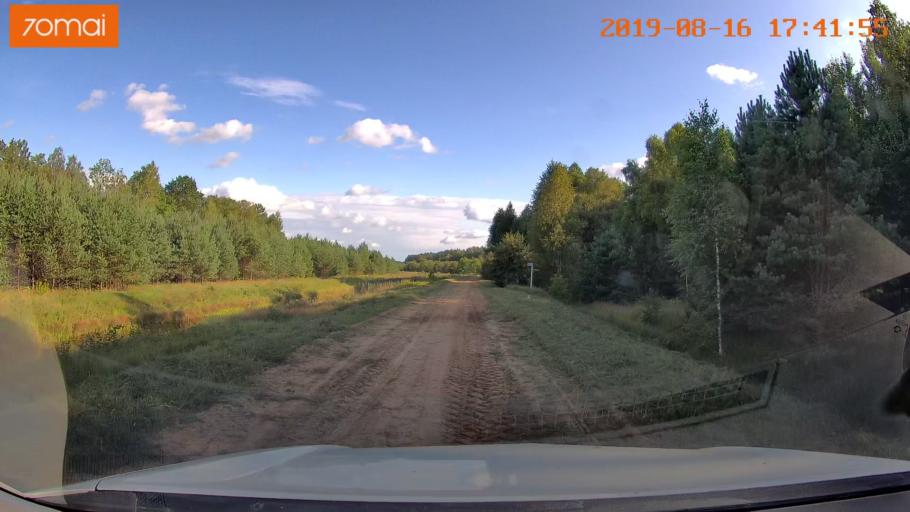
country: BY
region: Mogilev
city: Asipovichy
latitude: 53.2385
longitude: 28.6649
